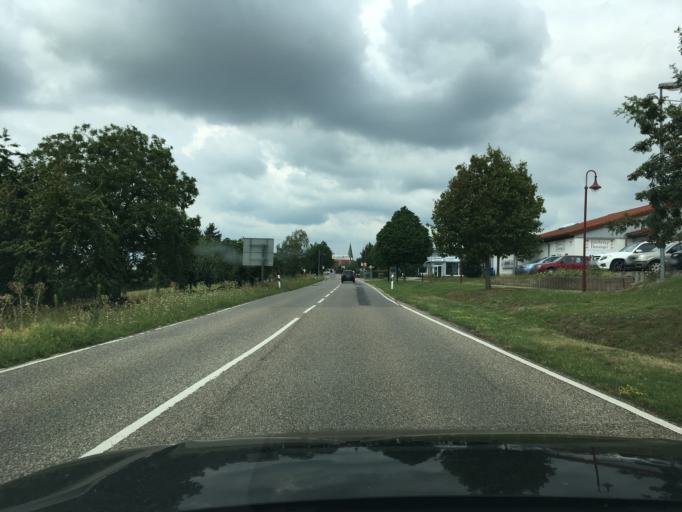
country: DE
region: Baden-Wuerttemberg
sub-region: Karlsruhe Region
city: Malsch
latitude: 49.2478
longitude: 8.6927
